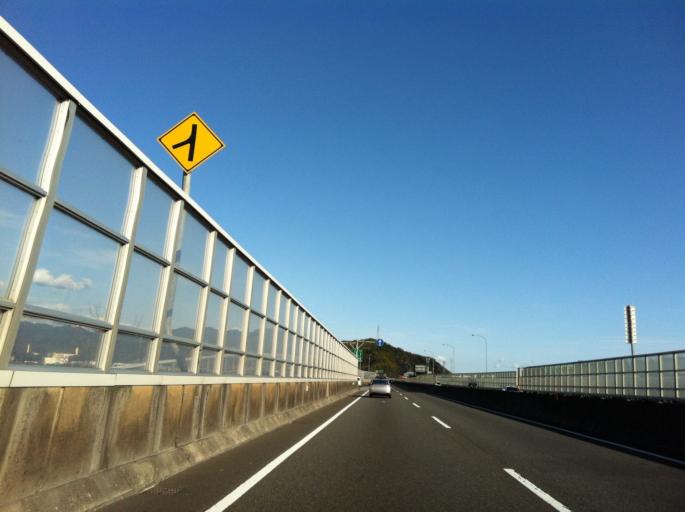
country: JP
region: Shizuoka
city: Shizuoka-shi
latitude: 35.0063
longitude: 138.3915
